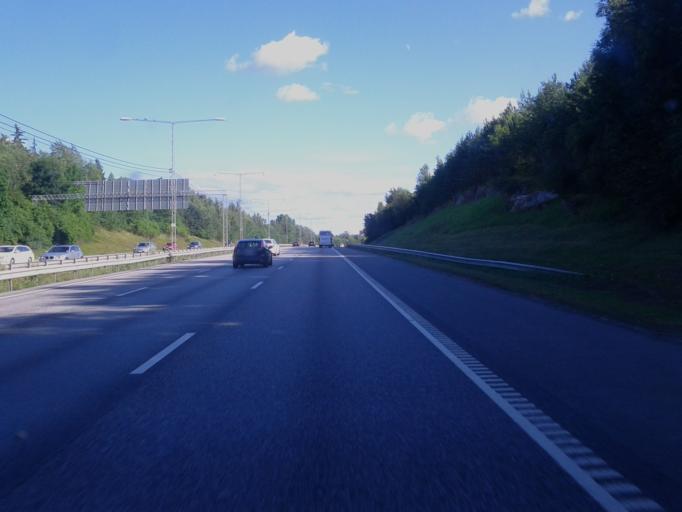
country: SE
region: Stockholm
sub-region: Sollentuna Kommun
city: Sollentuna
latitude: 59.4553
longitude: 17.9145
